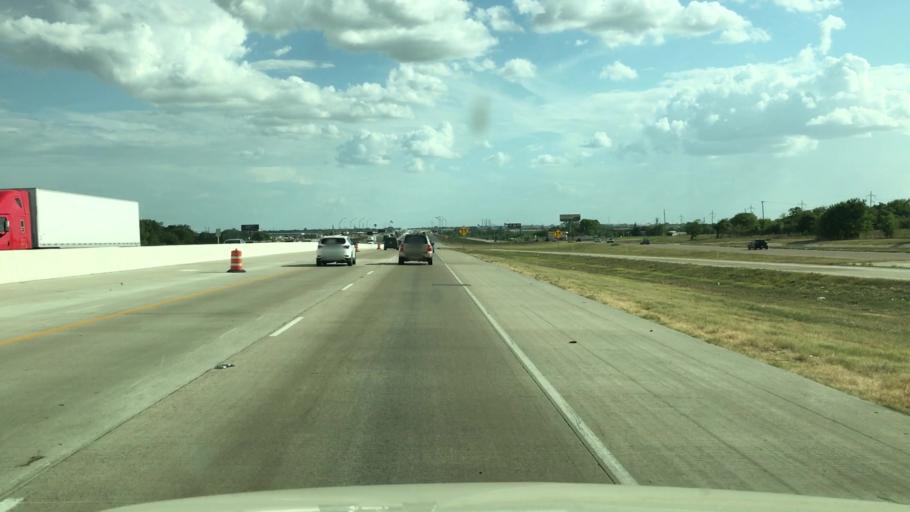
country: US
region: Texas
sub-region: Bell County
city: Troy
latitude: 31.1612
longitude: -97.3218
